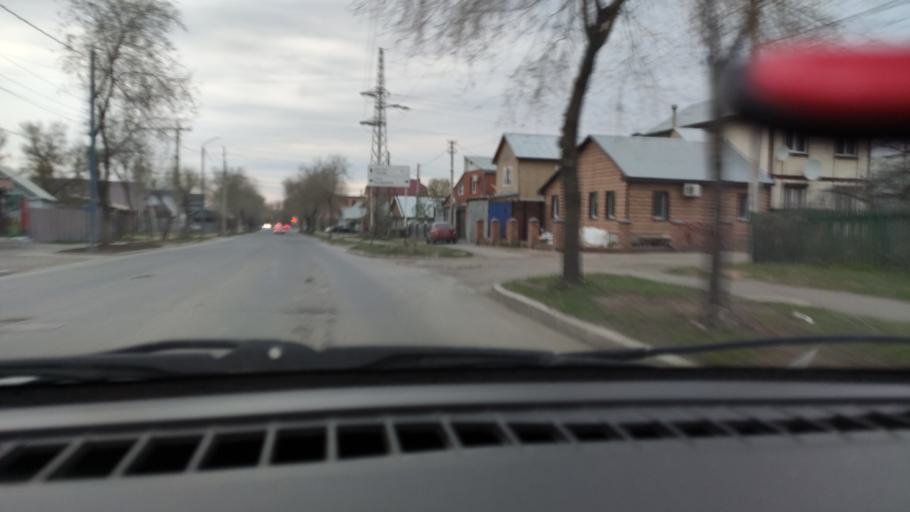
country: RU
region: Orenburg
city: Orenburg
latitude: 51.7791
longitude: 55.1142
